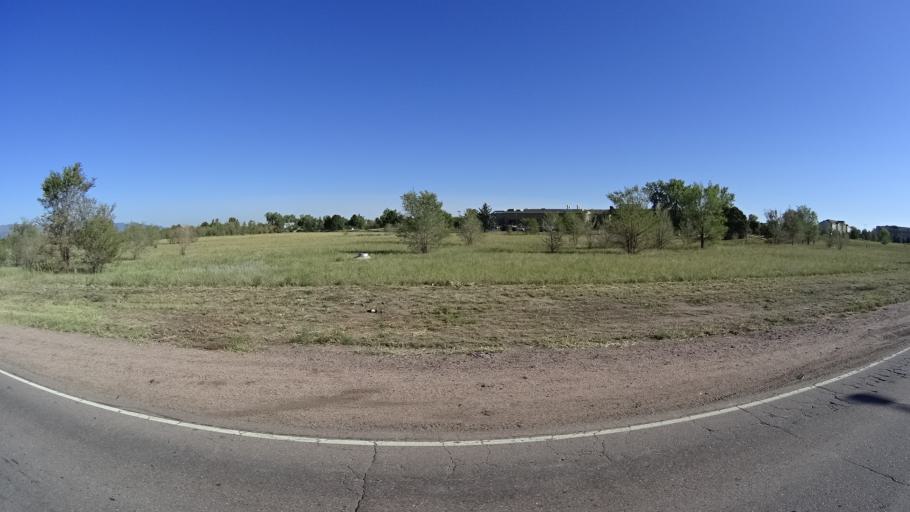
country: US
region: Colorado
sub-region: El Paso County
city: Stratmoor
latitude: 38.8063
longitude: -104.7333
